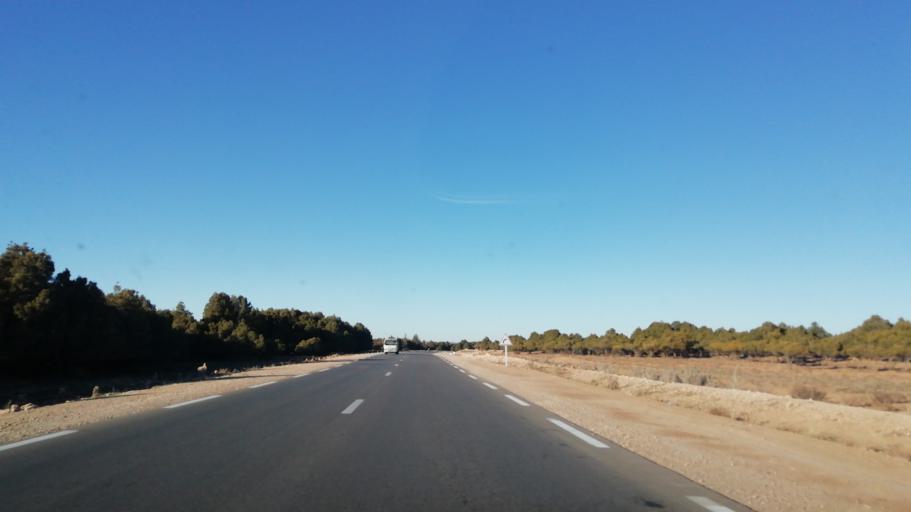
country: DZ
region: Tlemcen
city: Sebdou
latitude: 34.4558
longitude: -1.2754
